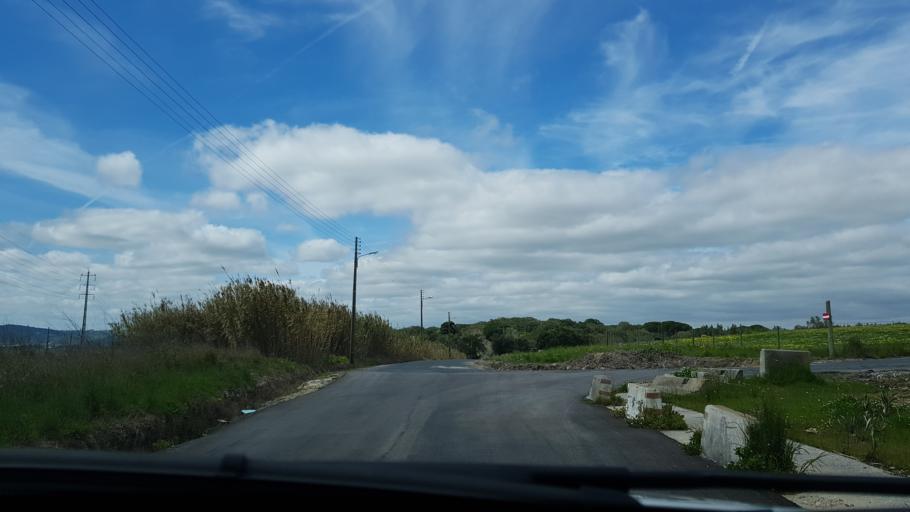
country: PT
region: Lisbon
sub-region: Alenquer
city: Carregado
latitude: 39.0446
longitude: -8.9277
